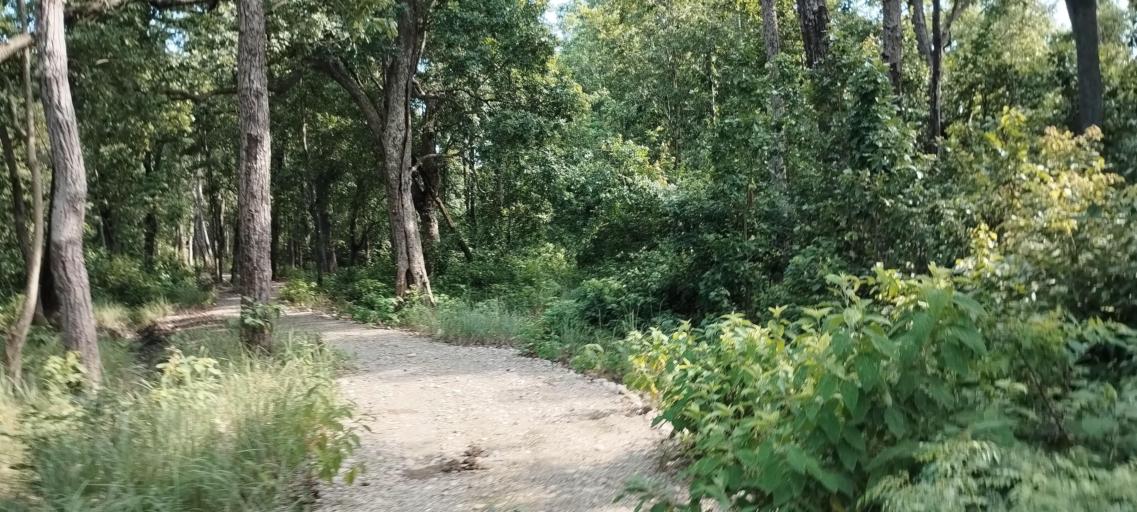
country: NP
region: Far Western
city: Tikapur
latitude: 28.5599
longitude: 81.2658
